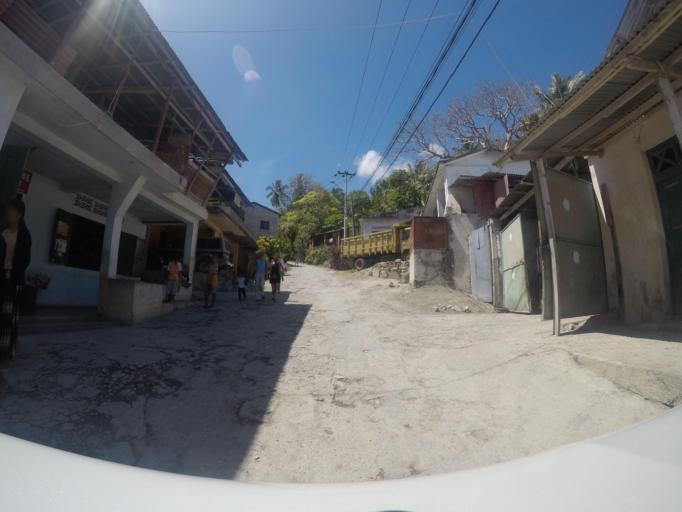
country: TL
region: Baucau
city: Baucau
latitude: -8.4639
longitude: 126.4522
